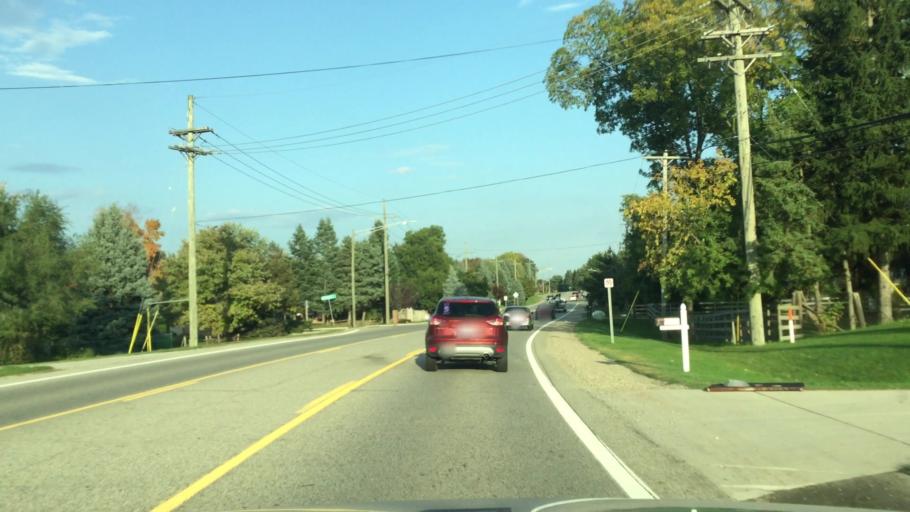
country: US
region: Michigan
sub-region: Oakland County
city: West Bloomfield Township
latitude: 42.6197
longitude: -83.4092
